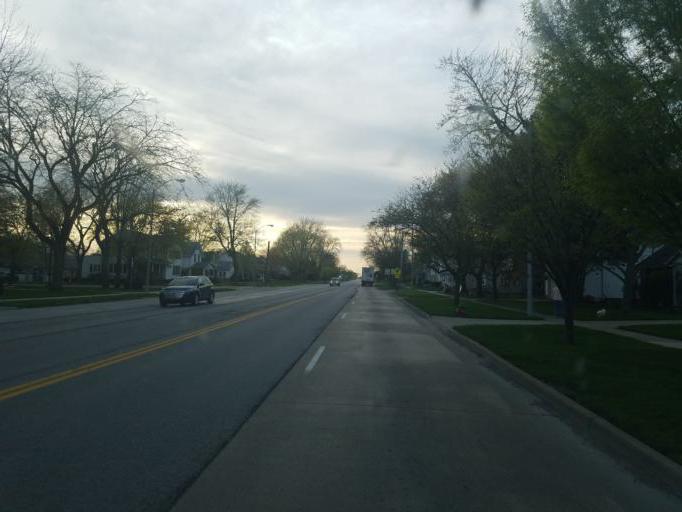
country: US
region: Ohio
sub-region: Sandusky County
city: Woodville
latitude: 41.4515
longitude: -83.3656
